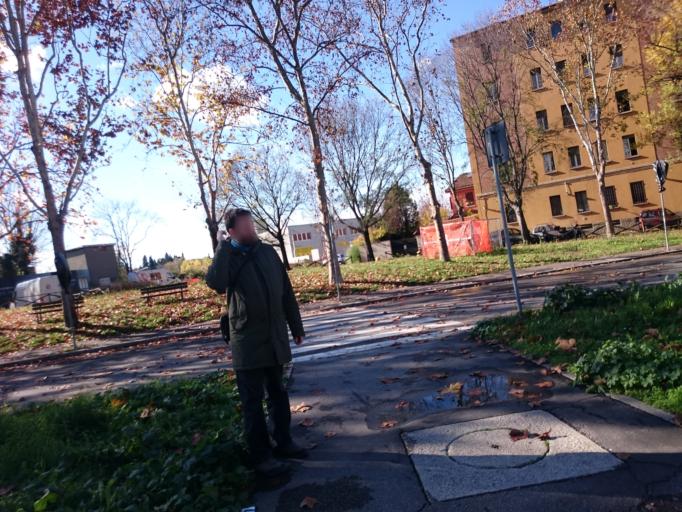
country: IT
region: Emilia-Romagna
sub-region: Provincia di Bologna
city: Bologna
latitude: 44.5168
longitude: 11.3364
